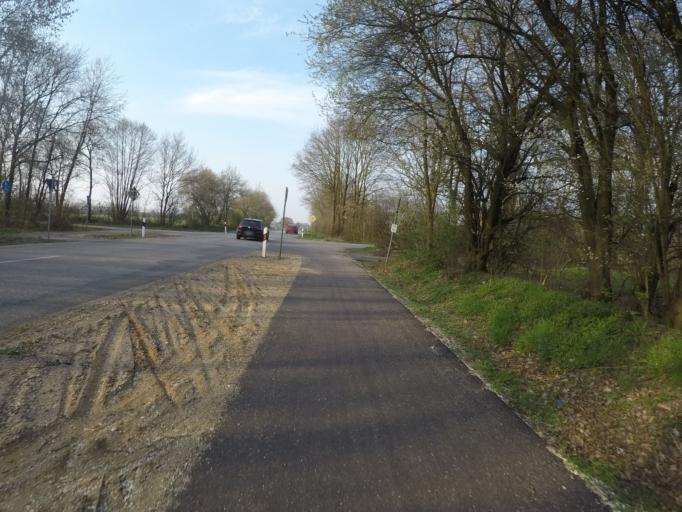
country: DE
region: Schleswig-Holstein
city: Wahlstedt
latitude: 53.9782
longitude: 10.1880
